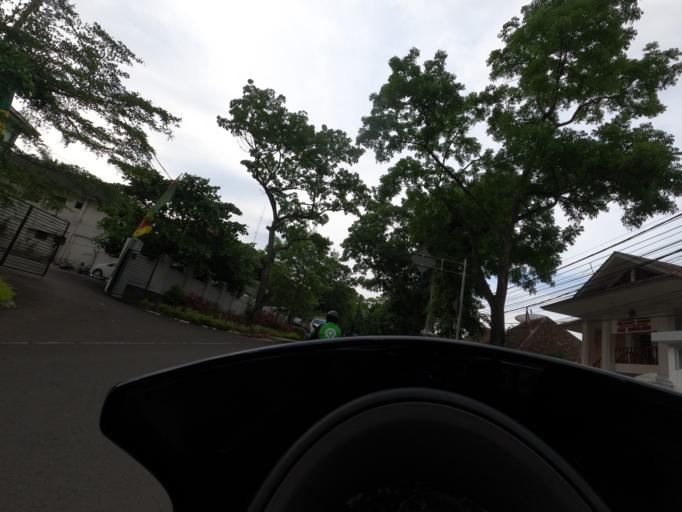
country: ID
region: West Java
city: Bandung
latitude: -6.9112
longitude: 107.6176
